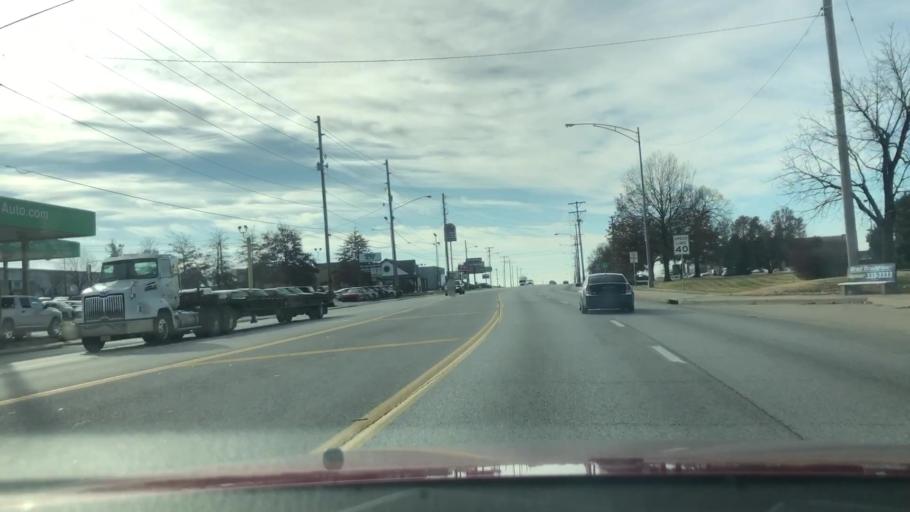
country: US
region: Missouri
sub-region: Greene County
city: Springfield
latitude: 37.2251
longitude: -93.2616
